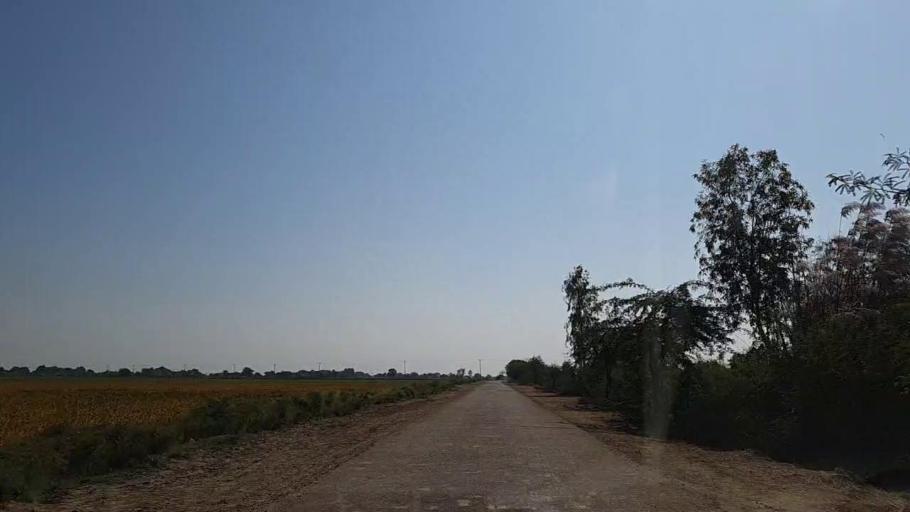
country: PK
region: Sindh
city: Chuhar Jamali
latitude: 24.5231
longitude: 68.0912
